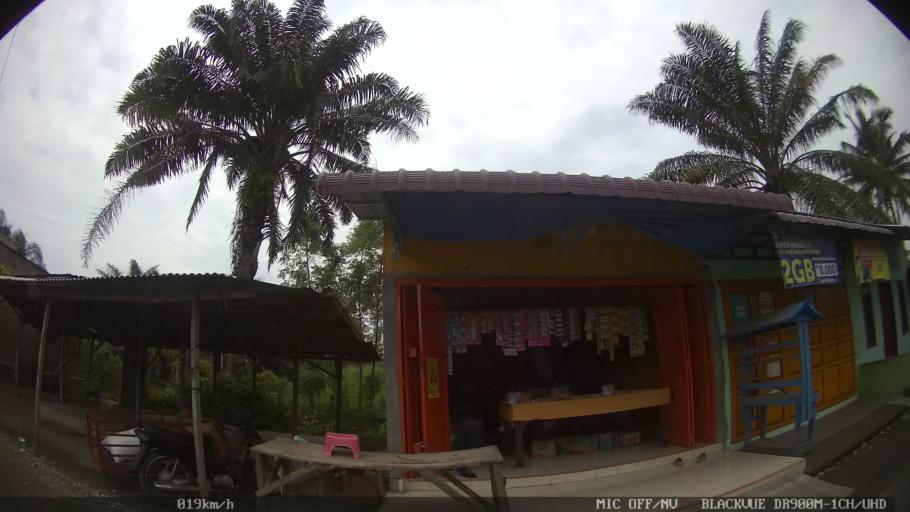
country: ID
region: North Sumatra
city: Sunggal
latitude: 3.6310
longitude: 98.5624
